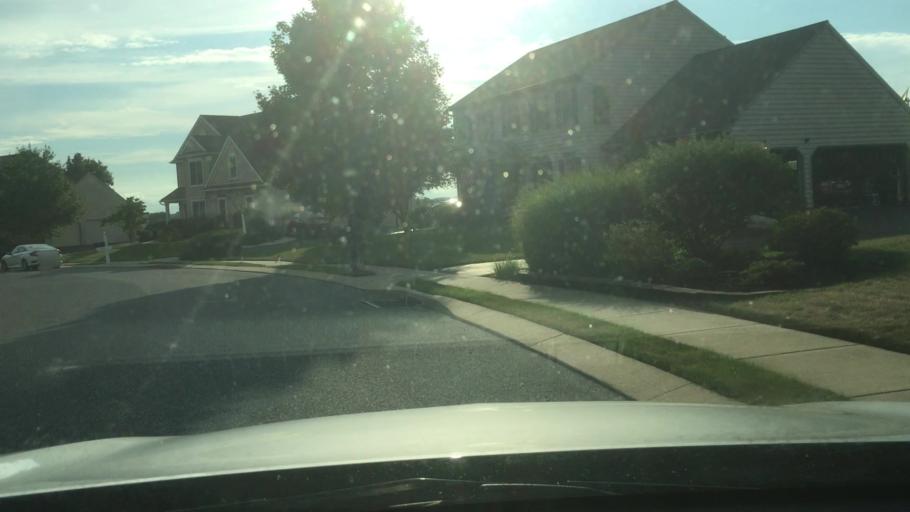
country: US
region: Pennsylvania
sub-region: York County
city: Shiloh
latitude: 39.9936
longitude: -76.7820
